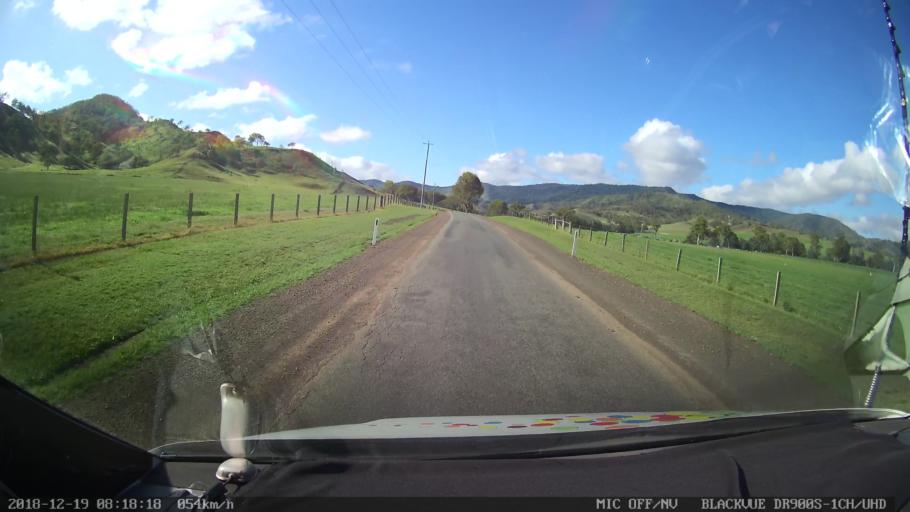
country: AU
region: New South Wales
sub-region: Kyogle
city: Kyogle
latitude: -28.2719
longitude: 152.9092
